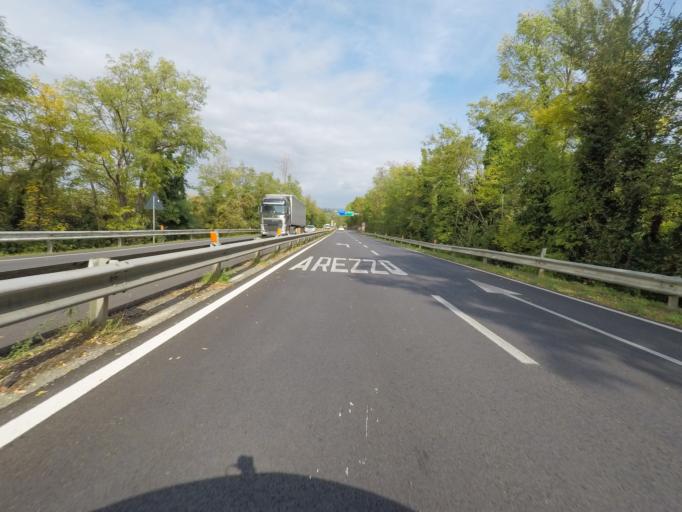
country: IT
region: Tuscany
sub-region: Provincia di Siena
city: Belverde
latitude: 43.3525
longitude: 11.3058
